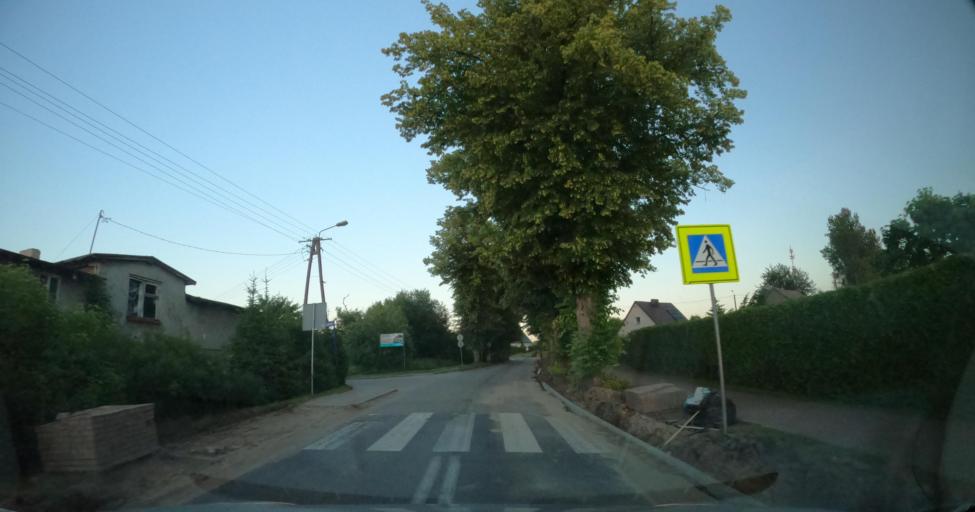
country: PL
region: Pomeranian Voivodeship
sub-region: Powiat wejherowski
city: Linia
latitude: 54.4518
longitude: 17.9268
